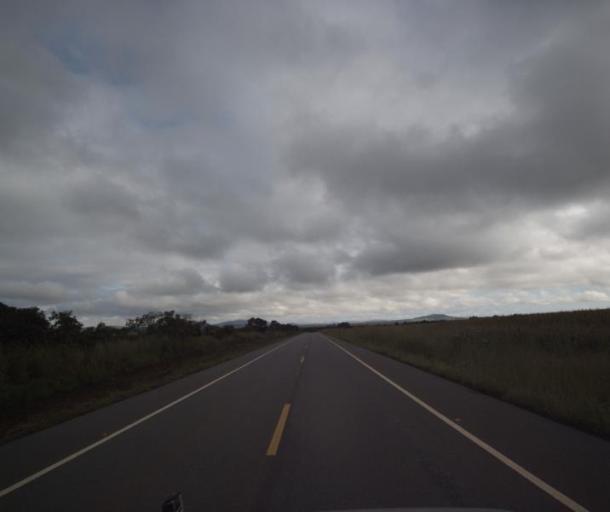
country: BR
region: Goias
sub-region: Padre Bernardo
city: Padre Bernardo
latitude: -15.3246
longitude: -48.6545
